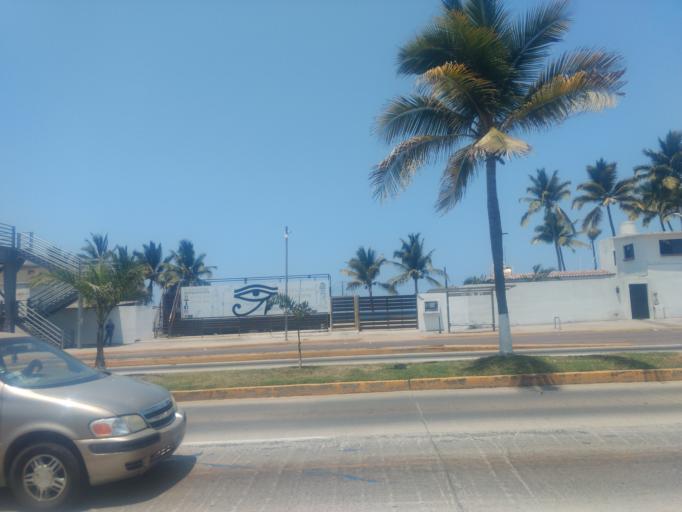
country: MX
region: Colima
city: Tapeixtles
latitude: 19.0907
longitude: -104.3141
